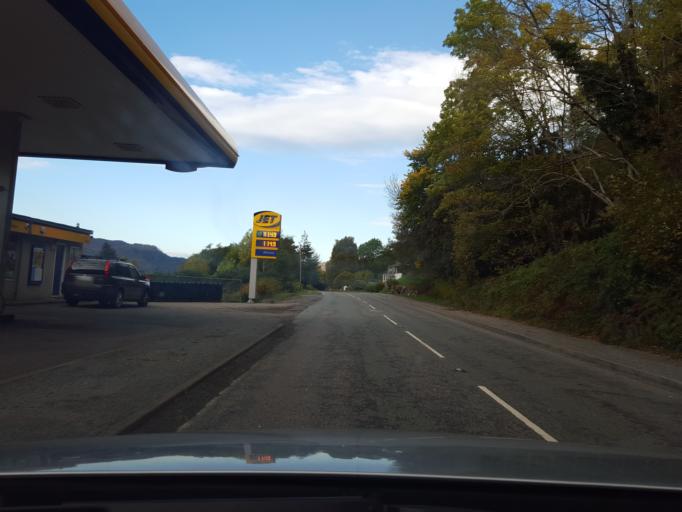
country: GB
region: Scotland
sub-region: Highland
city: Fort William
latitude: 57.2422
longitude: -5.4578
